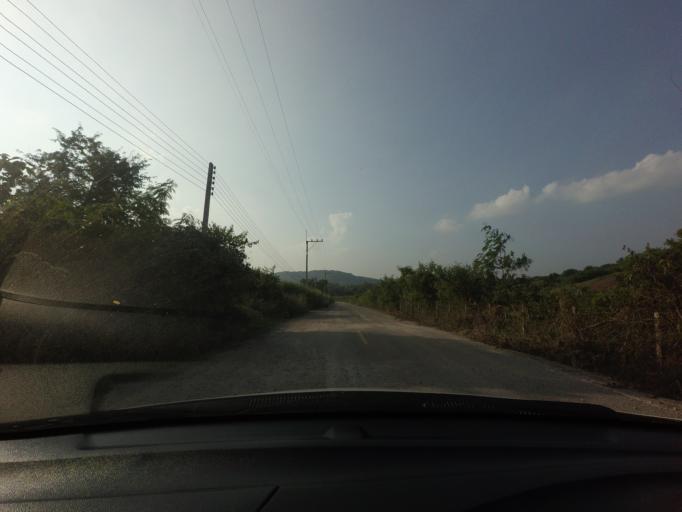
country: TH
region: Nakhon Ratchasima
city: Pak Chong
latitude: 14.5399
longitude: 101.5802
